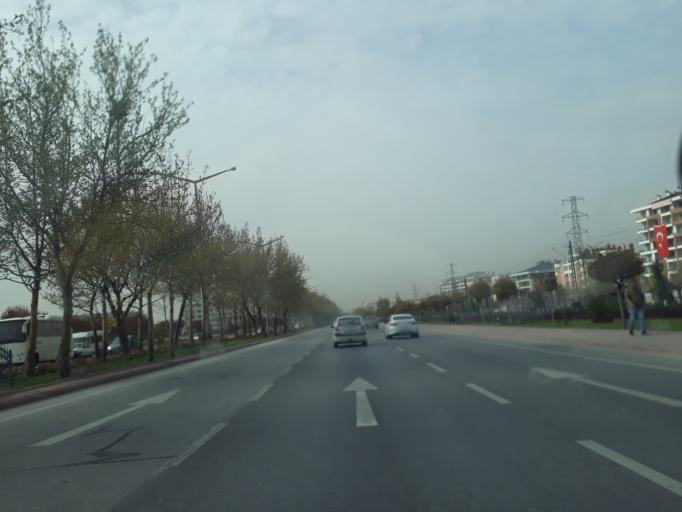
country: TR
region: Konya
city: Selcuklu
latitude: 37.9760
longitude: 32.5164
